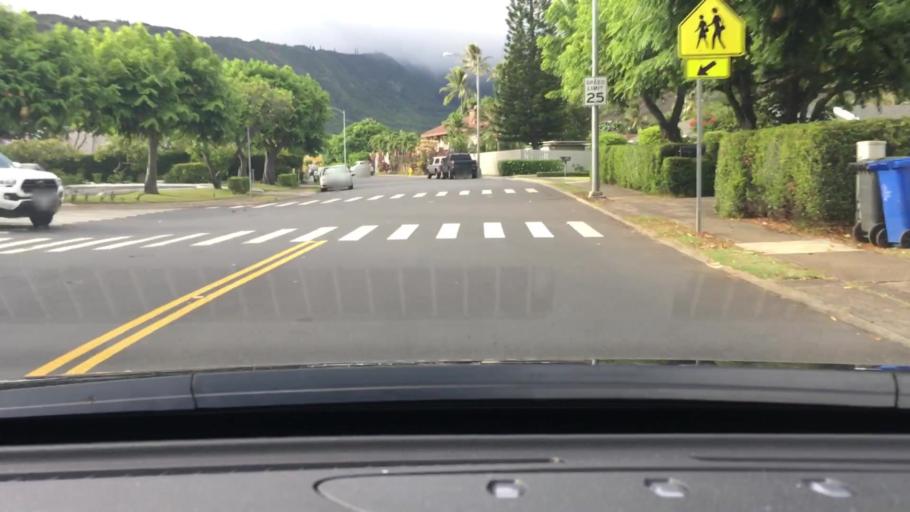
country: US
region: Hawaii
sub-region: Honolulu County
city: Waimanalo
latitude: 21.2787
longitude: -157.7517
